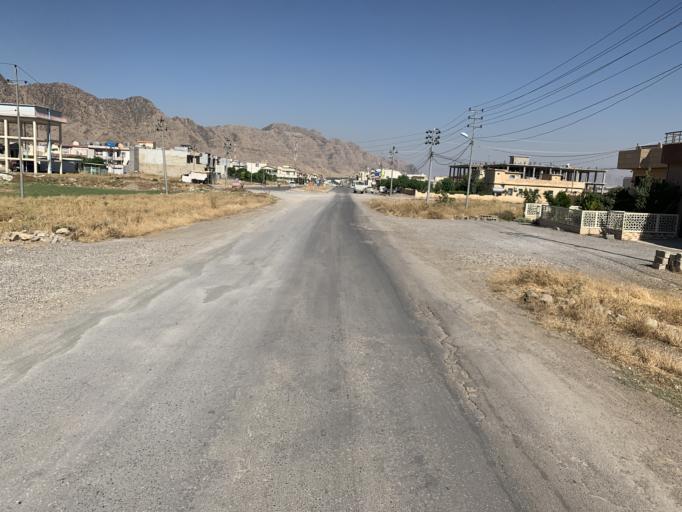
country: IQ
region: As Sulaymaniyah
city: Raniye
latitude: 36.2598
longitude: 44.8609
